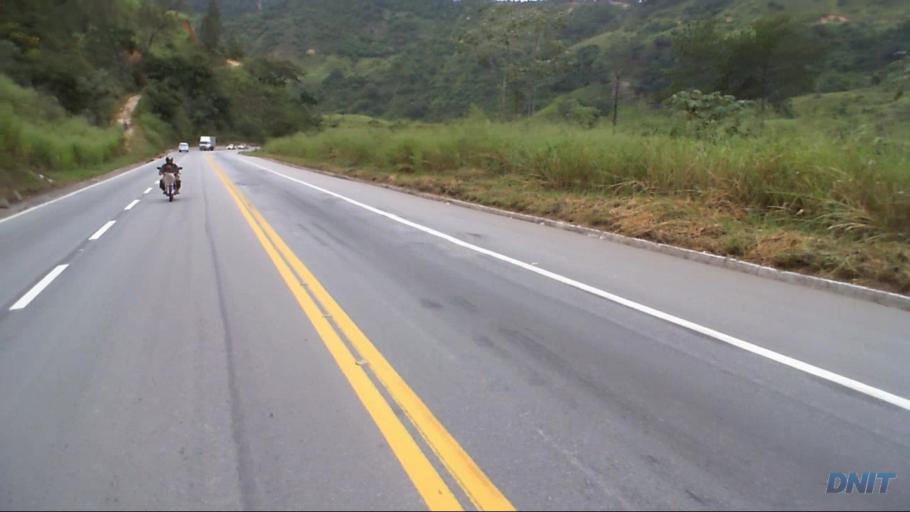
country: BR
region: Minas Gerais
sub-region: Timoteo
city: Timoteo
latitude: -19.6389
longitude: -42.8128
